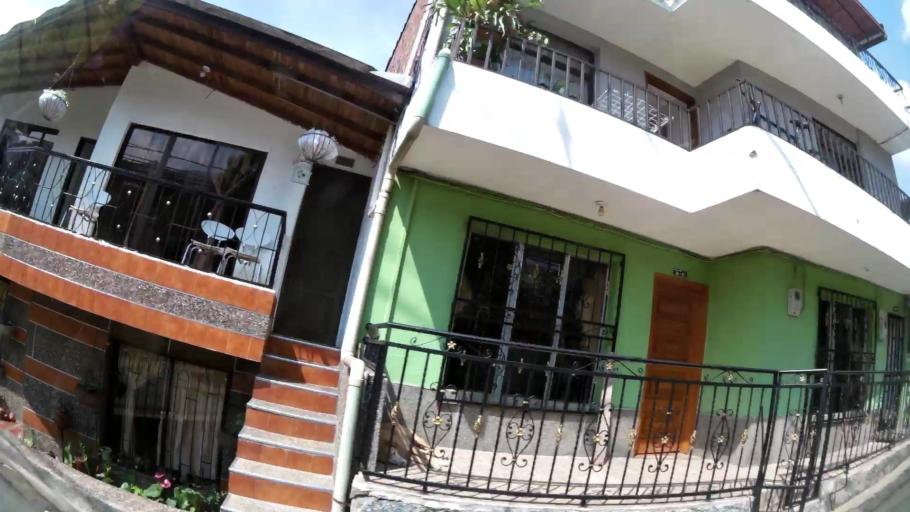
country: CO
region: Antioquia
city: La Estrella
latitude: 6.1872
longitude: -75.6414
